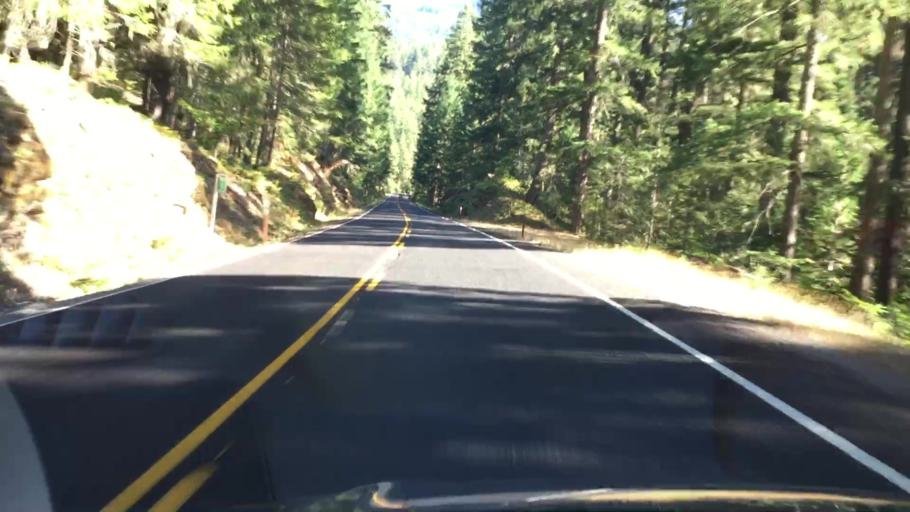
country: US
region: Washington
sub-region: Pierce County
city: Buckley
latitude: 46.6976
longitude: -121.5817
